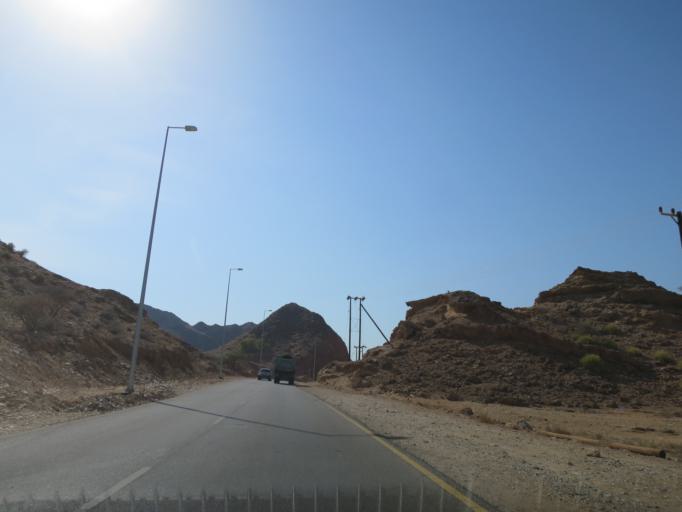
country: OM
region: Muhafazat Masqat
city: Muscat
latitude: 23.5163
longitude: 58.7131
